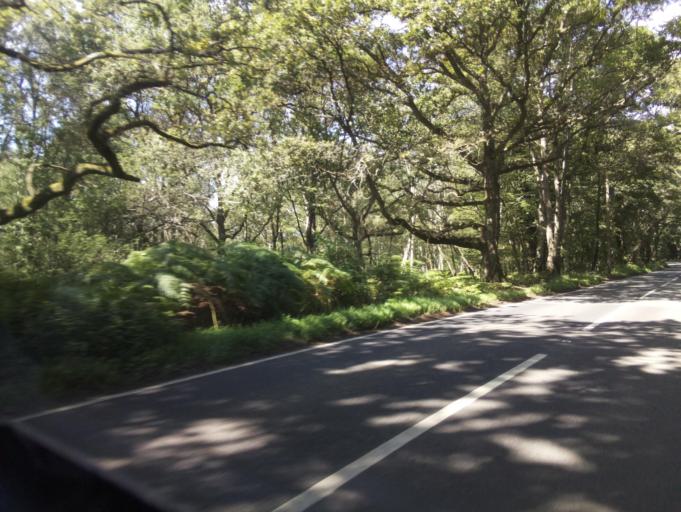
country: GB
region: England
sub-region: West Berkshire
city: Winterbourne
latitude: 51.4311
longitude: -1.3334
